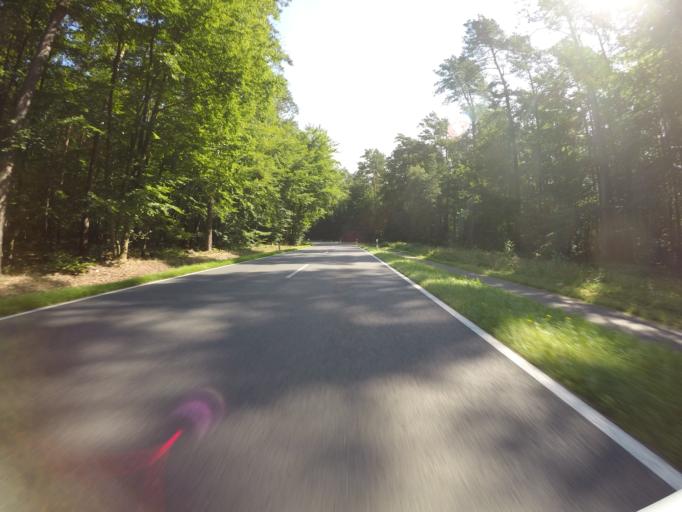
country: DE
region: Brandenburg
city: Rheinsberg
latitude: 53.1114
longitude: 12.9824
